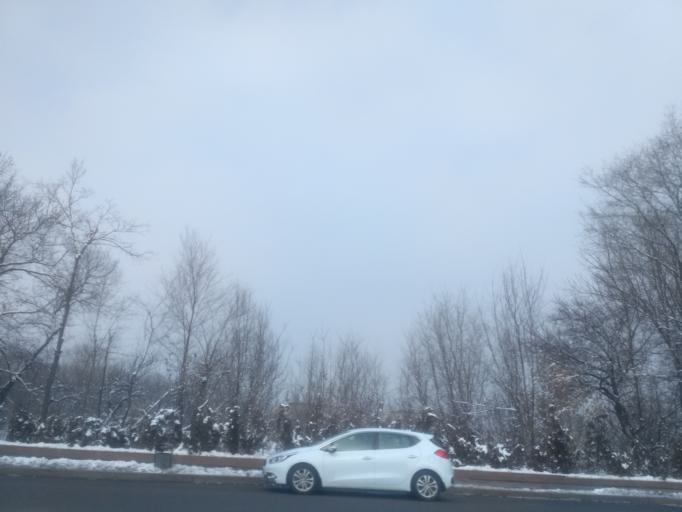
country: KZ
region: Almaty Qalasy
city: Almaty
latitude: 43.2170
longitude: 76.9271
